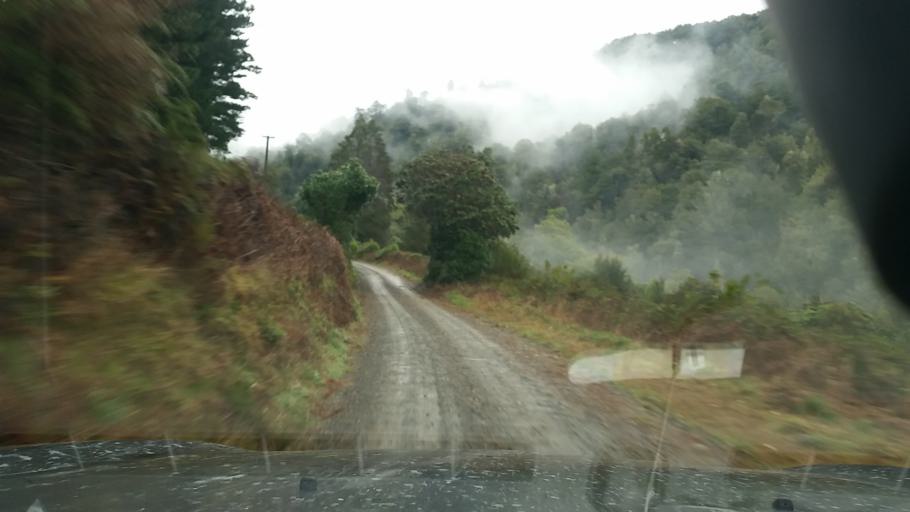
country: NZ
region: Nelson
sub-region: Nelson City
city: Nelson
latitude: -41.3632
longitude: 173.6052
